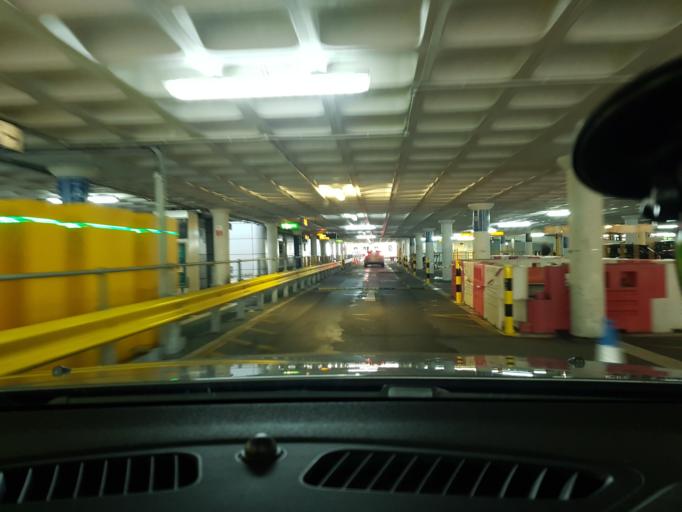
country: GB
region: England
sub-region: Surrey
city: Horley
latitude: 51.1606
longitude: -0.1761
